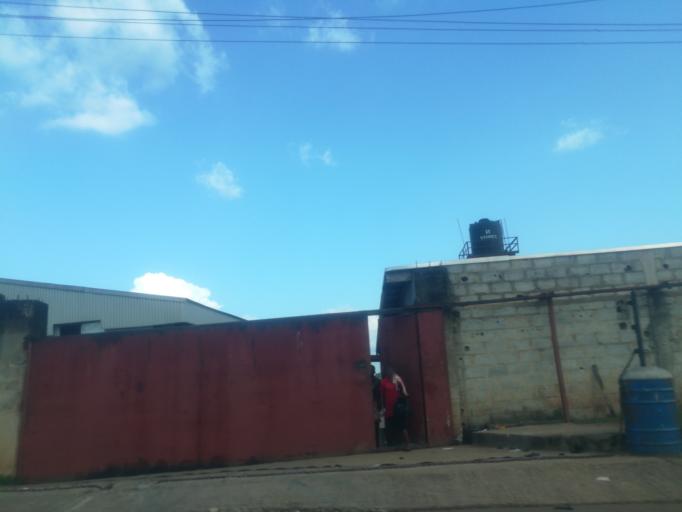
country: NG
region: Oyo
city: Ibadan
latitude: 7.4006
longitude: 3.9631
